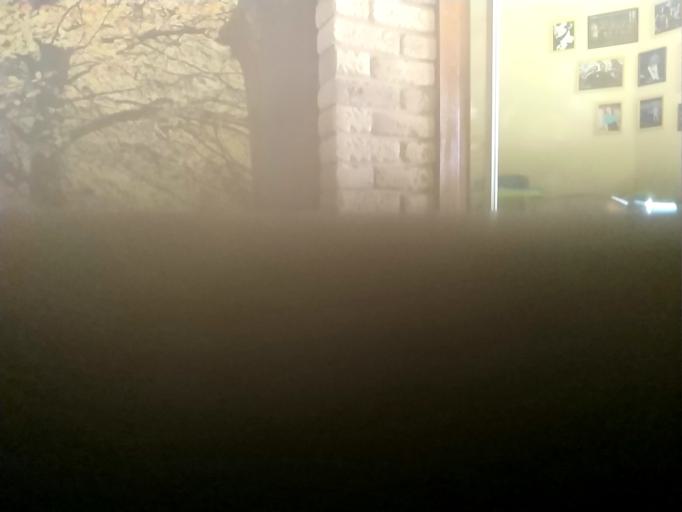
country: RU
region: Kaluga
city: Yukhnov
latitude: 54.7819
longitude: 35.0205
